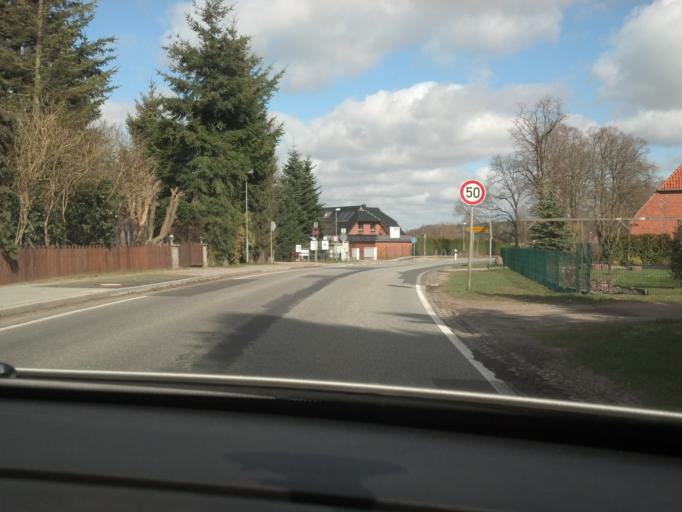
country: DE
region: Mecklenburg-Vorpommern
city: Boizenburg
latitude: 53.3976
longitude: 10.7486
